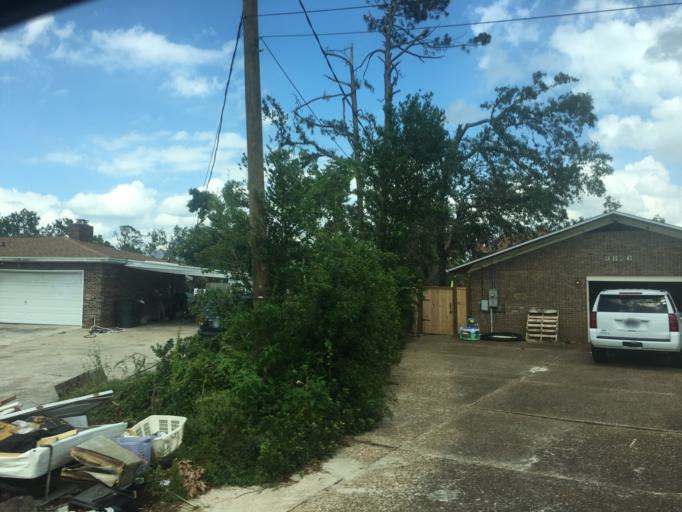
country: US
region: Florida
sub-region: Bay County
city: Pretty Bayou
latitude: 30.1959
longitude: -85.7083
